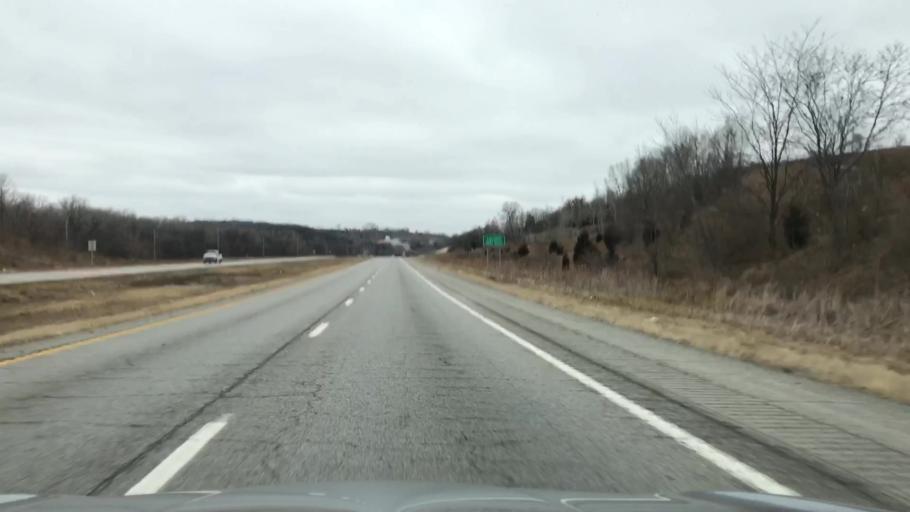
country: US
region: Missouri
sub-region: Jackson County
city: East Independence
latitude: 39.1367
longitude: -94.3858
